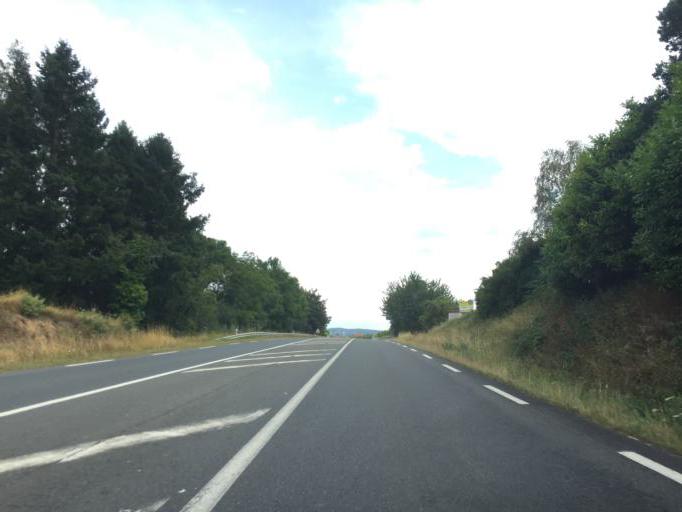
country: FR
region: Rhone-Alpes
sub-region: Departement de la Loire
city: Saint-Symphorien-de-Lay
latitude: 45.9510
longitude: 4.1999
